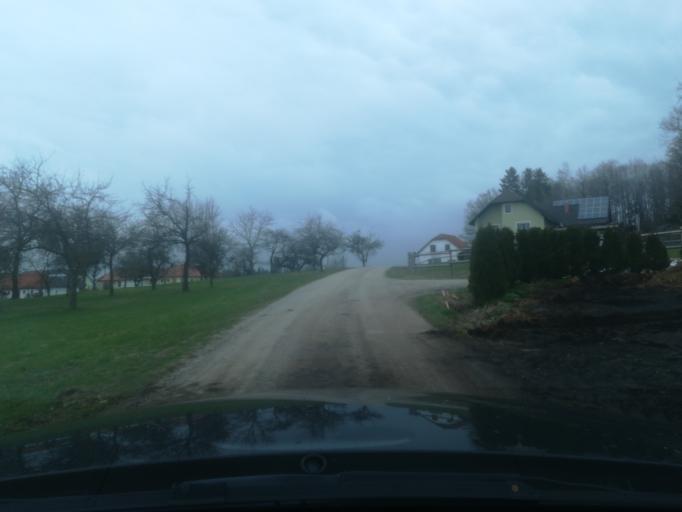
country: AT
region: Upper Austria
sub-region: Politischer Bezirk Rohrbach
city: Kleinzell im Muehlkreis
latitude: 48.3705
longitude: 13.9181
